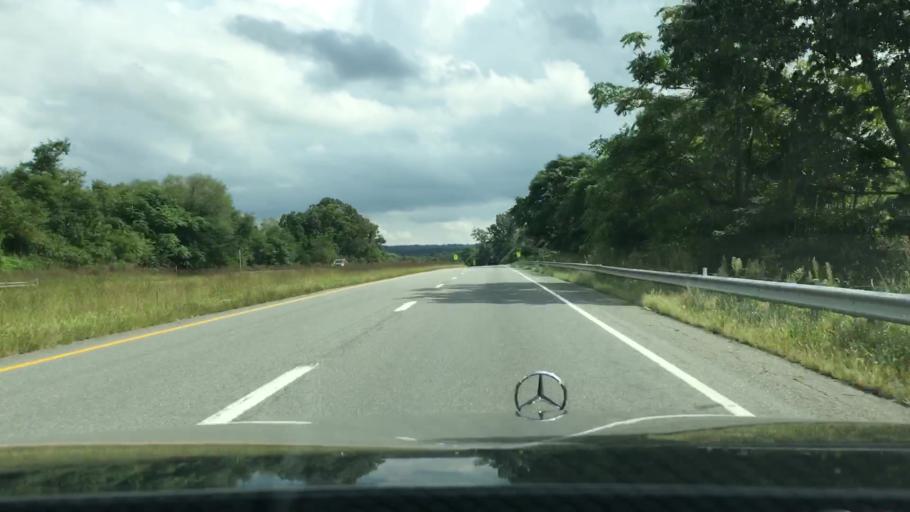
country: US
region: Virginia
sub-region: Frederick County
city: Shawnee Land
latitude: 39.2787
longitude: -78.2555
